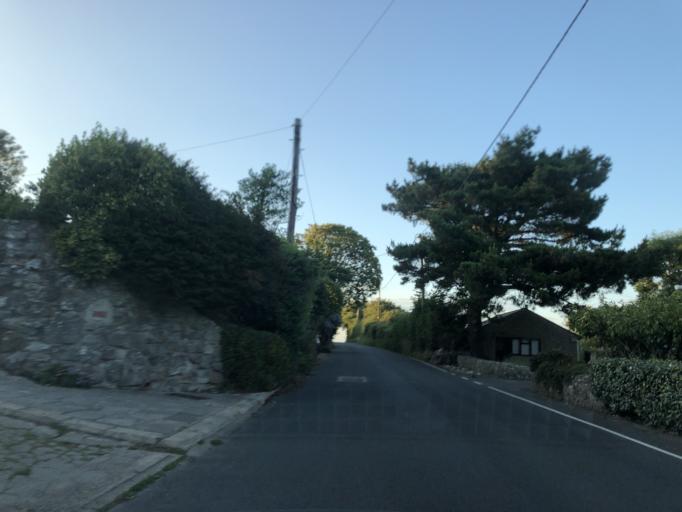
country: GB
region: England
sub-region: Isle of Wight
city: Niton
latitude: 50.5979
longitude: -1.2793
